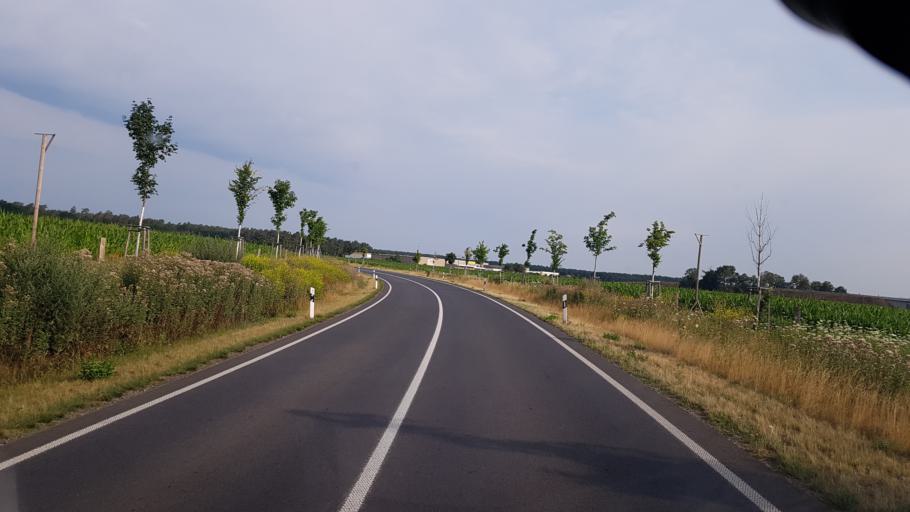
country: DE
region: Brandenburg
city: Golssen
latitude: 51.9772
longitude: 13.5706
